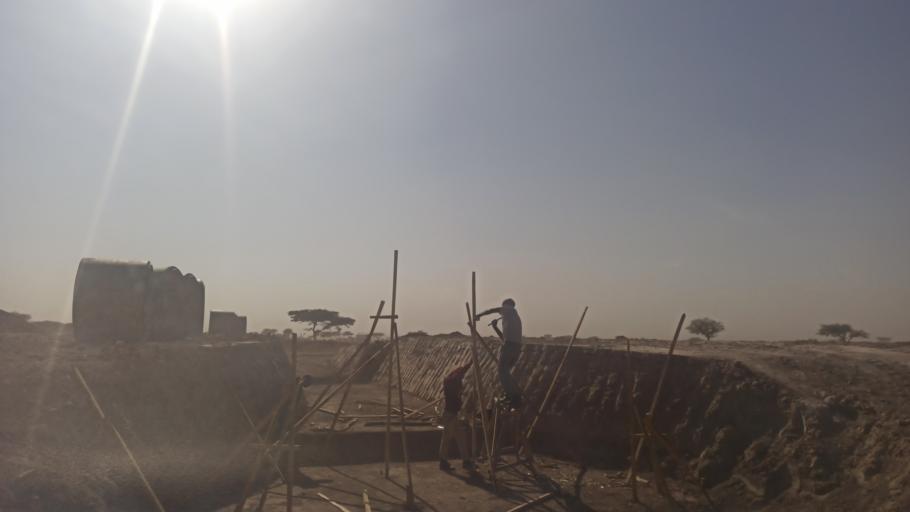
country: ET
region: Oromiya
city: Ziway
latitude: 7.7372
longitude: 38.6223
